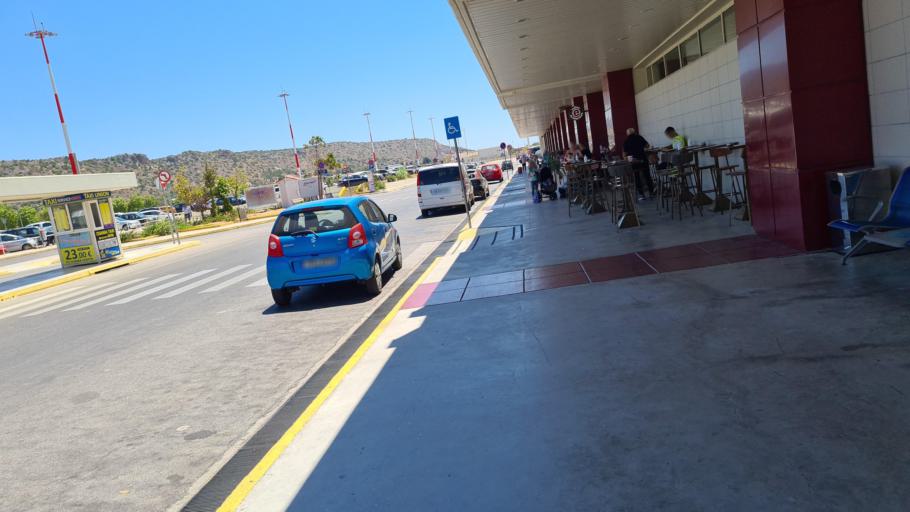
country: GR
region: Crete
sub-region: Nomos Chanias
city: Mouzouras
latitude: 35.5403
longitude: 24.1406
